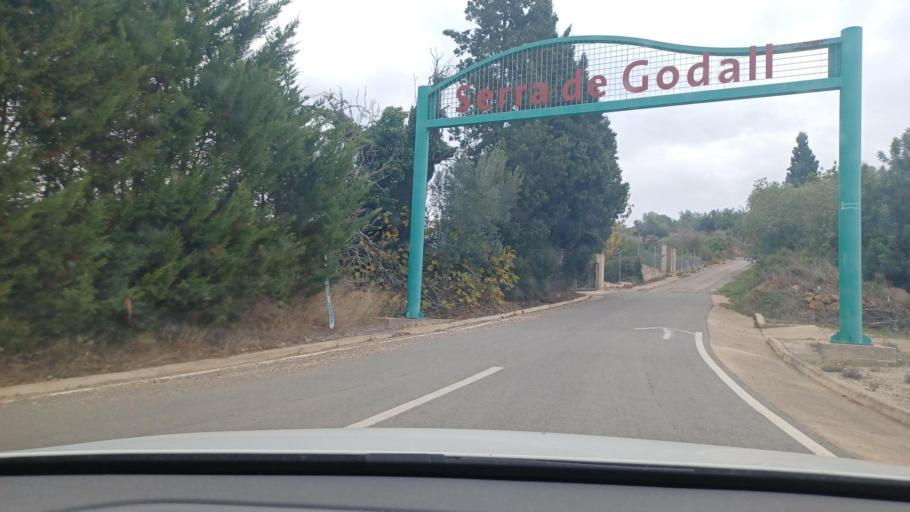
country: ES
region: Catalonia
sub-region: Provincia de Tarragona
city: Ulldecona
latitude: 40.6507
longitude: 0.4667
